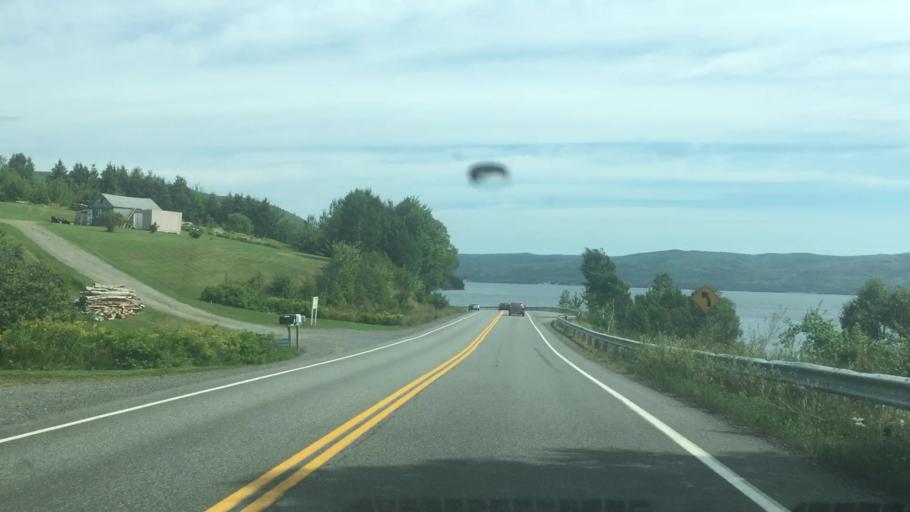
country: CA
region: Nova Scotia
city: Sydney Mines
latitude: 46.2654
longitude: -60.6125
